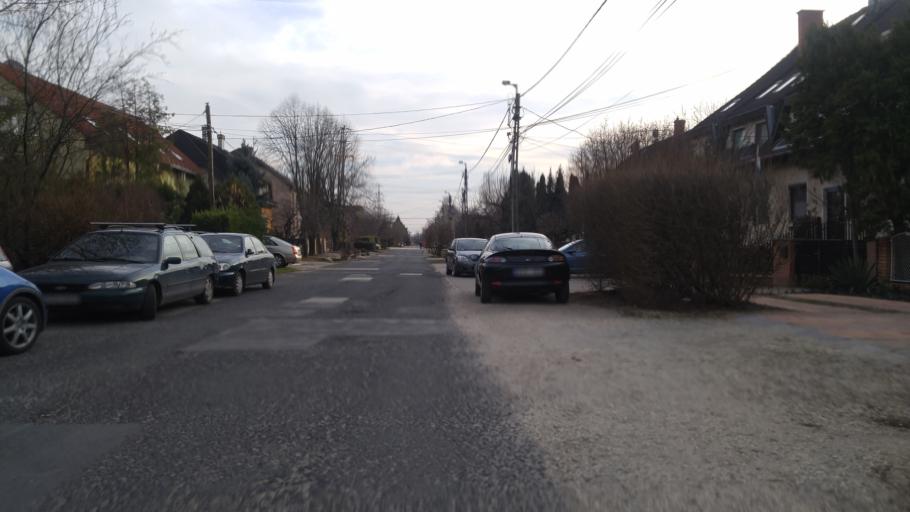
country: HU
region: Budapest
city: Budapest XVII. keruelet
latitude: 47.4772
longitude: 19.2334
